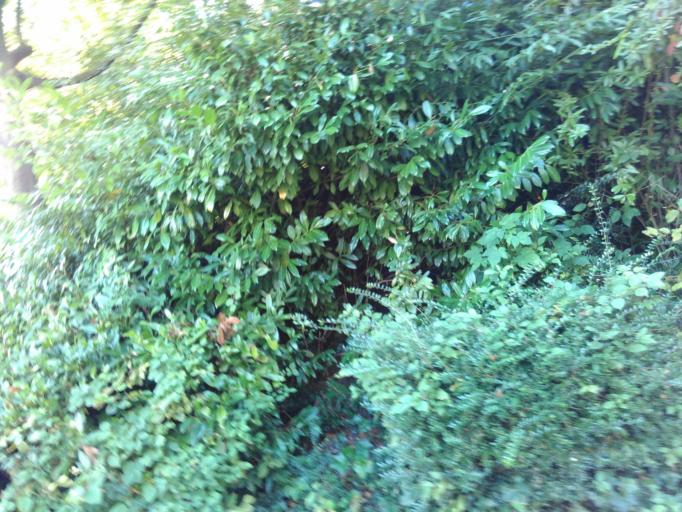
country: BE
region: Brussels Capital
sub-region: Bruxelles-Capitale
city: Brussels
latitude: 50.8206
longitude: 4.3978
